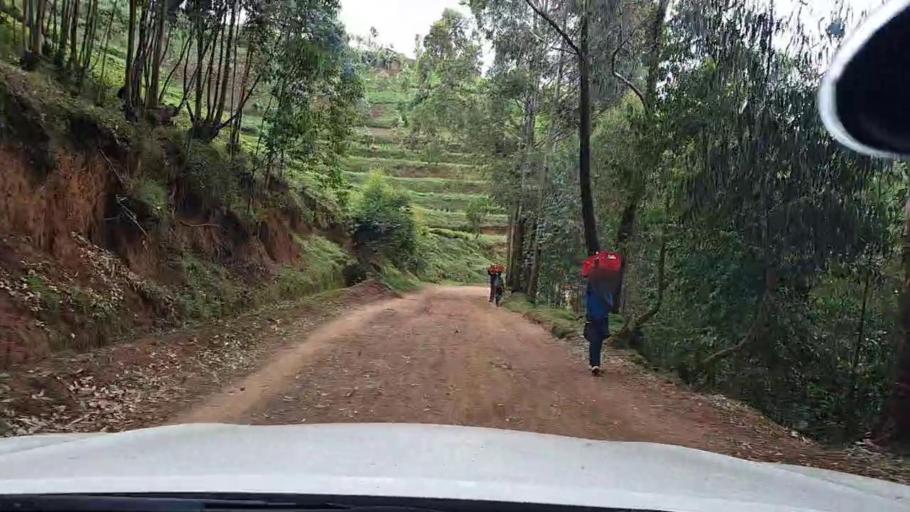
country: RW
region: Western Province
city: Kibuye
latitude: -2.1694
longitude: 29.4254
